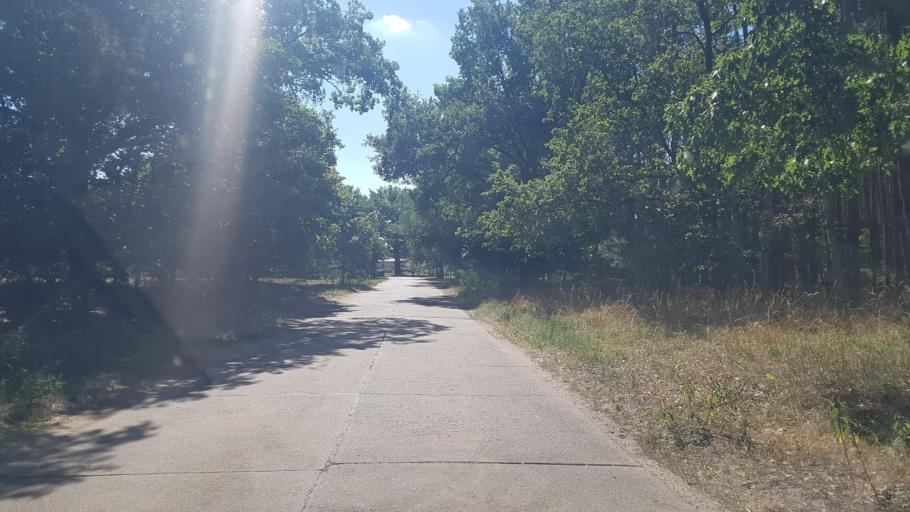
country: DE
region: Brandenburg
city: Golzow
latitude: 52.2970
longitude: 12.5838
